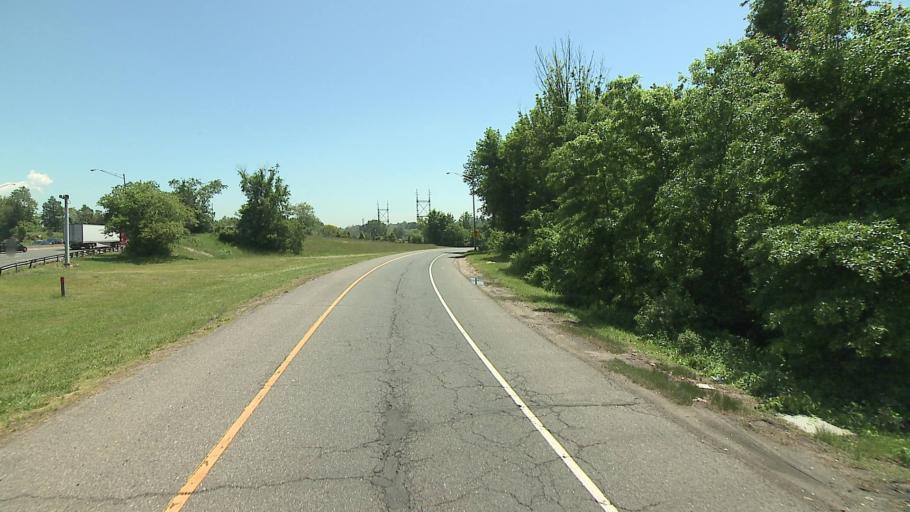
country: US
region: Connecticut
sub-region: Fairfield County
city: East Norwalk
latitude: 41.1197
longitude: -73.3777
